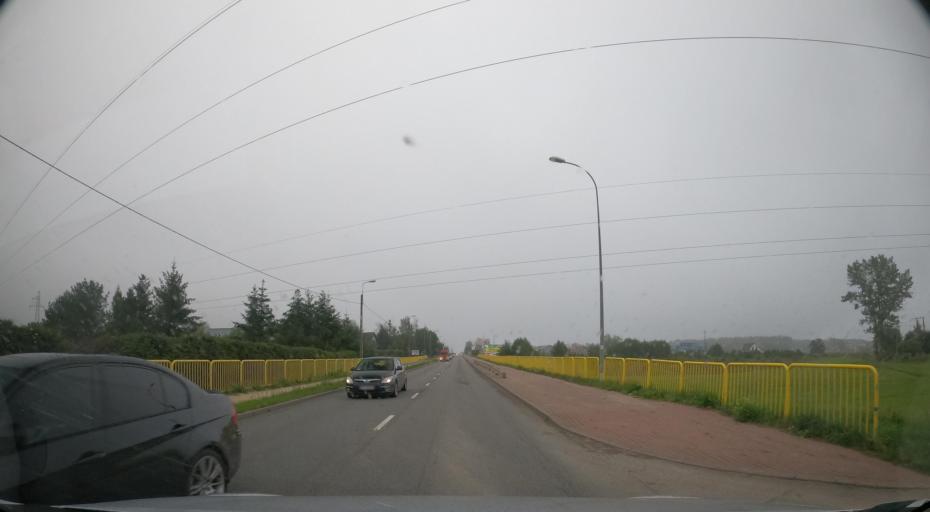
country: PL
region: Pomeranian Voivodeship
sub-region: Powiat kartuski
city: Chwaszczyno
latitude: 54.4432
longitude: 18.4035
